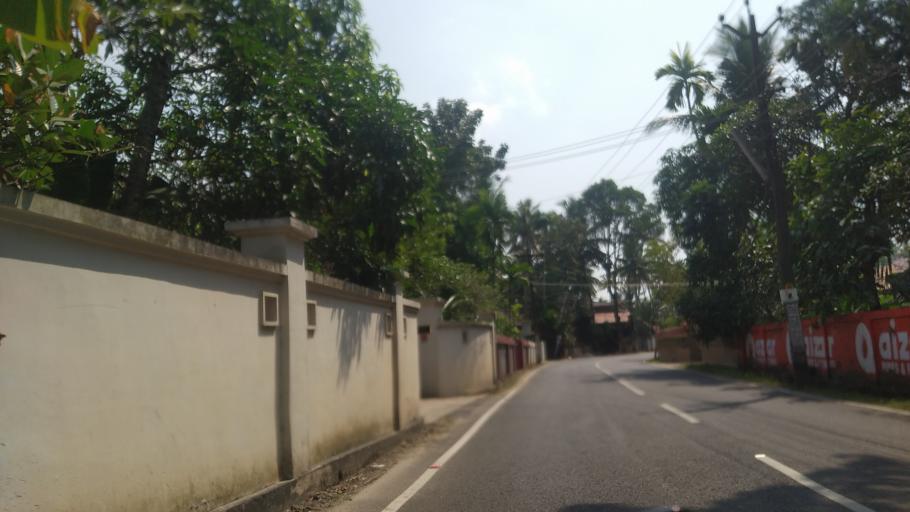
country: IN
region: Kerala
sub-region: Ernakulam
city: Elur
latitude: 10.1337
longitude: 76.2324
